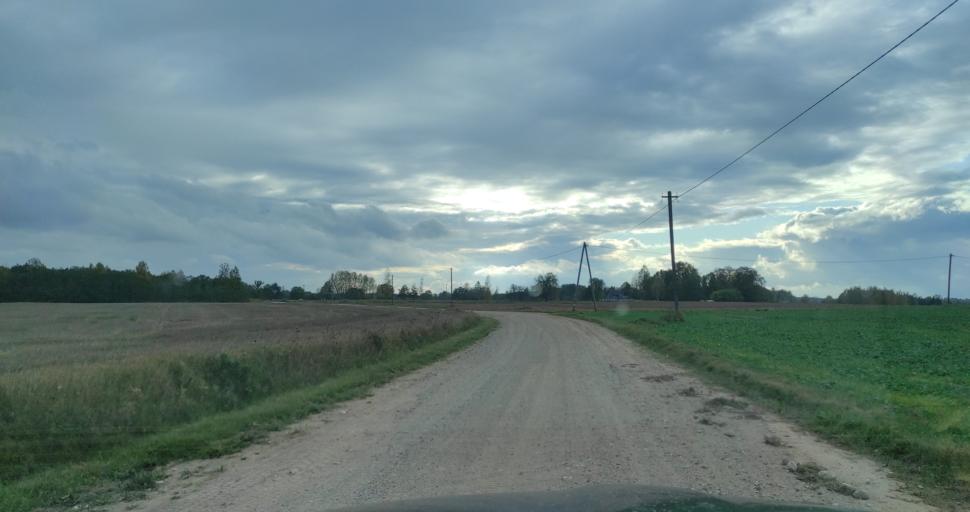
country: LV
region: Talsu Rajons
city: Sabile
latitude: 56.8999
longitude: 22.4297
